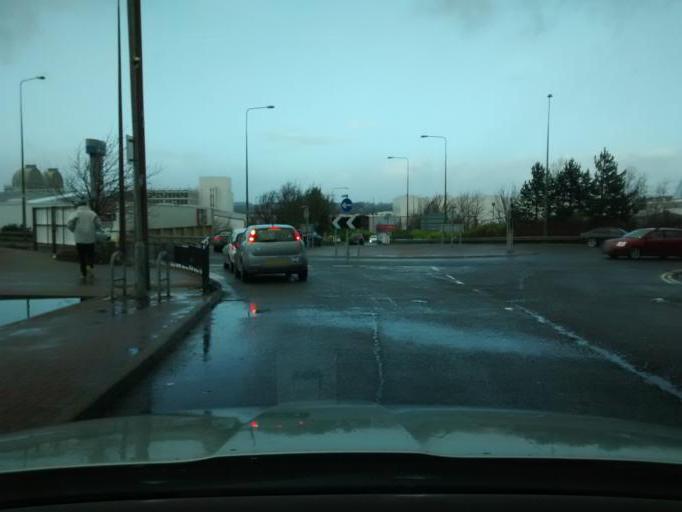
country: GB
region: Scotland
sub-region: West Lothian
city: Livingston
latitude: 55.8804
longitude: -3.5187
